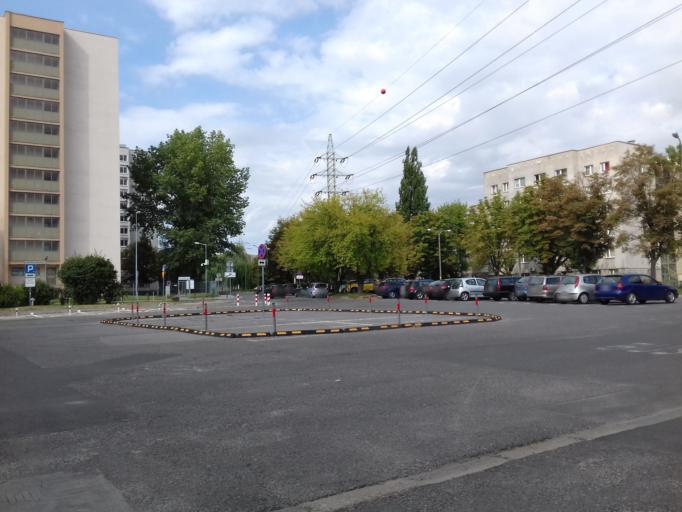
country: PL
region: Lesser Poland Voivodeship
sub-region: Krakow
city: Krakow
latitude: 50.0838
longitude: 19.9965
